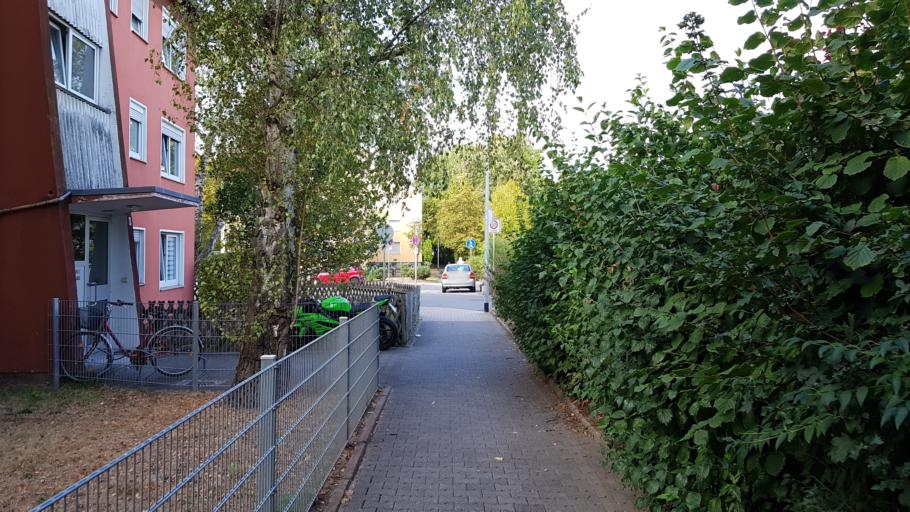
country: DE
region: Hesse
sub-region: Regierungsbezirk Darmstadt
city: Russelsheim
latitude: 49.9941
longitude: 8.4357
